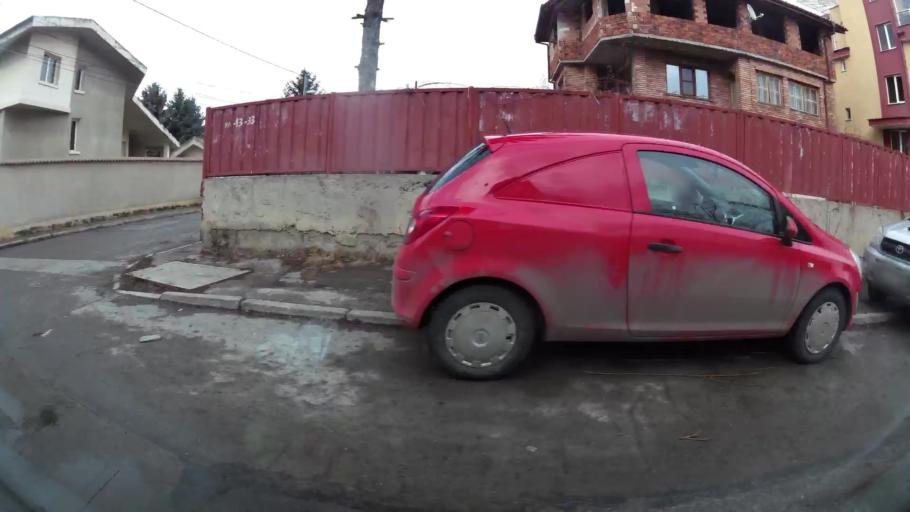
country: BG
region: Sofiya
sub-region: Obshtina Bozhurishte
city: Bozhurishte
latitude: 42.7449
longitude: 23.2672
